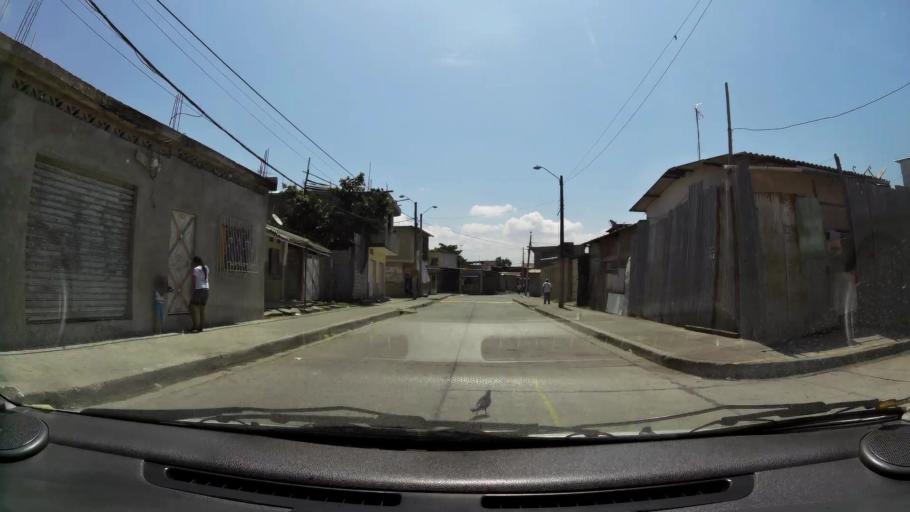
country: EC
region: Guayas
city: Guayaquil
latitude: -2.2377
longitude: -79.9163
